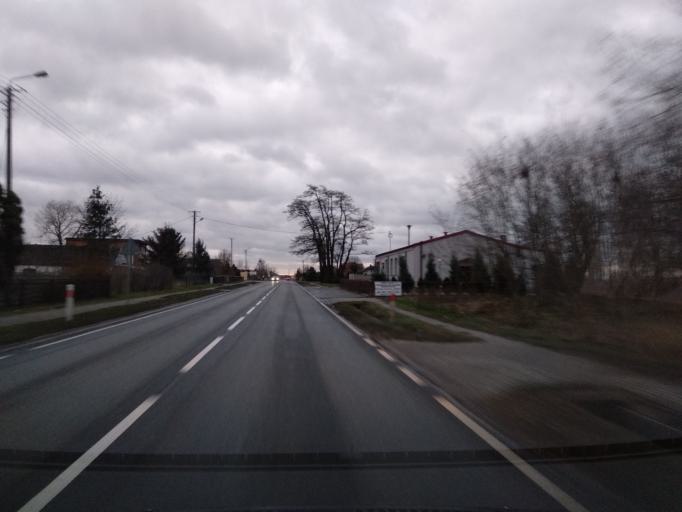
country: PL
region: Greater Poland Voivodeship
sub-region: Powiat koninski
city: Rychwal
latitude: 52.1207
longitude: 18.1696
